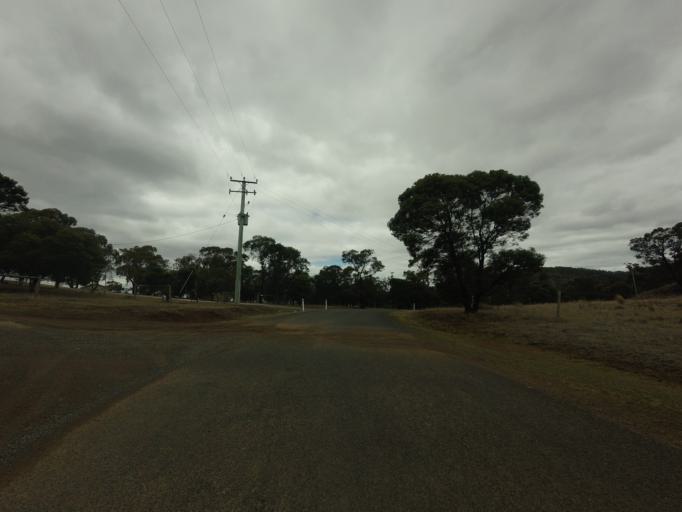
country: AU
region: Tasmania
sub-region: Clarence
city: Cambridge
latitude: -42.7905
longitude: 147.4023
